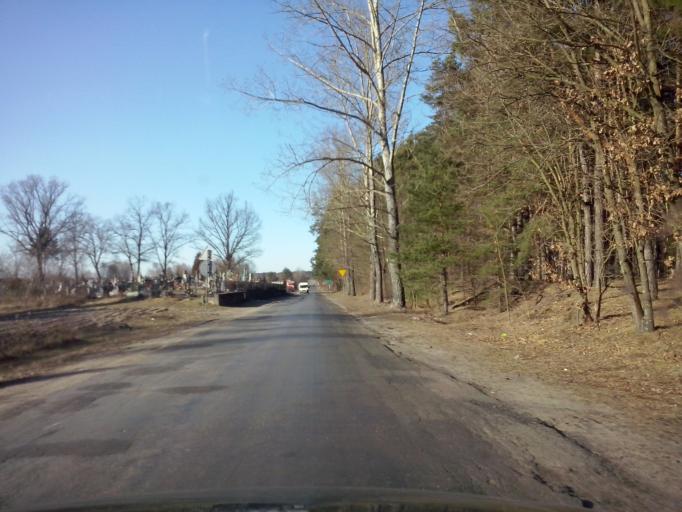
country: PL
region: Subcarpathian Voivodeship
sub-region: Powiat nizanski
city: Harasiuki
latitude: 50.5158
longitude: 22.4551
